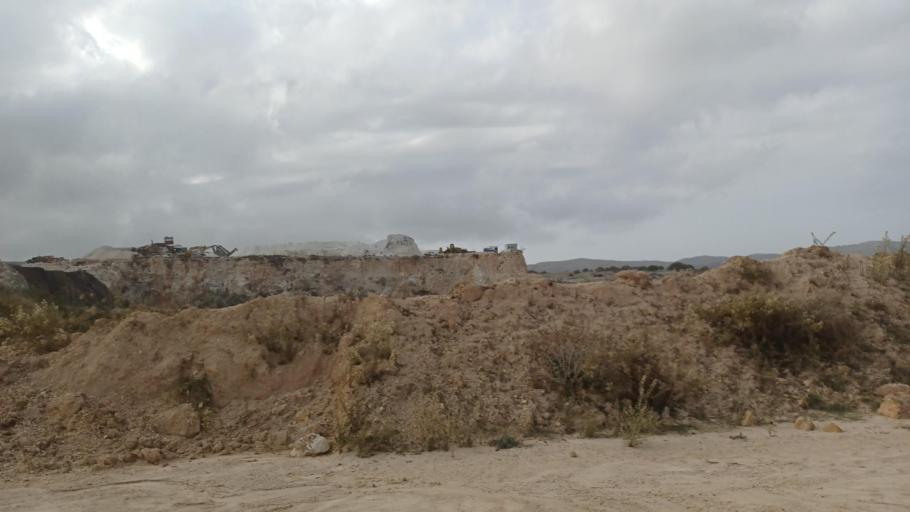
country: CY
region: Pafos
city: Polis
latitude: 35.0041
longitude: 32.3899
